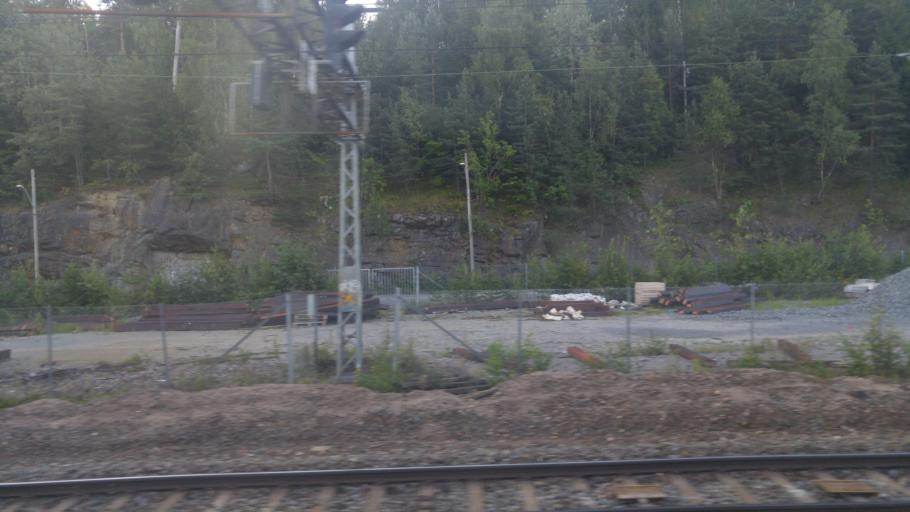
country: NO
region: Oslo
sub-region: Oslo
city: Oslo
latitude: 59.9096
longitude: 10.8226
